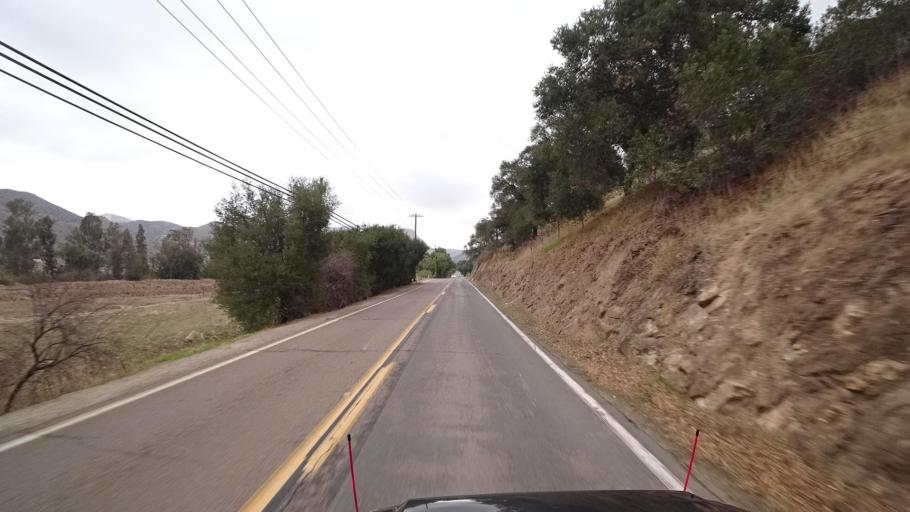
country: US
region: California
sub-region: San Diego County
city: Lakeside
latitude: 32.8734
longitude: -116.8799
